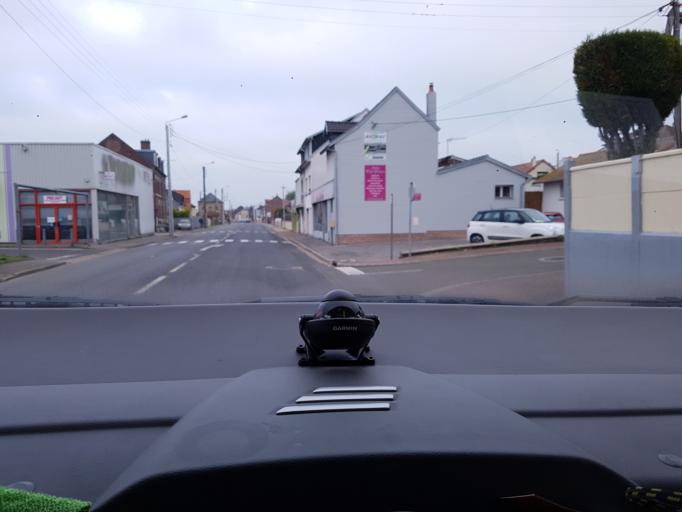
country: FR
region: Picardie
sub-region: Departement de la Somme
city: Mers-les-Bains
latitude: 50.0628
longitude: 1.4024
